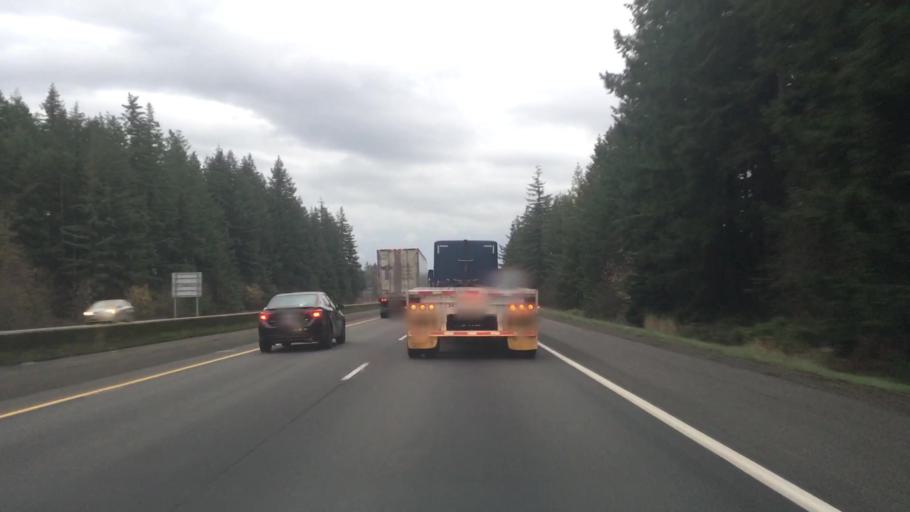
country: US
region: Washington
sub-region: Lewis County
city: Napavine
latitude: 46.5362
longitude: -122.8768
